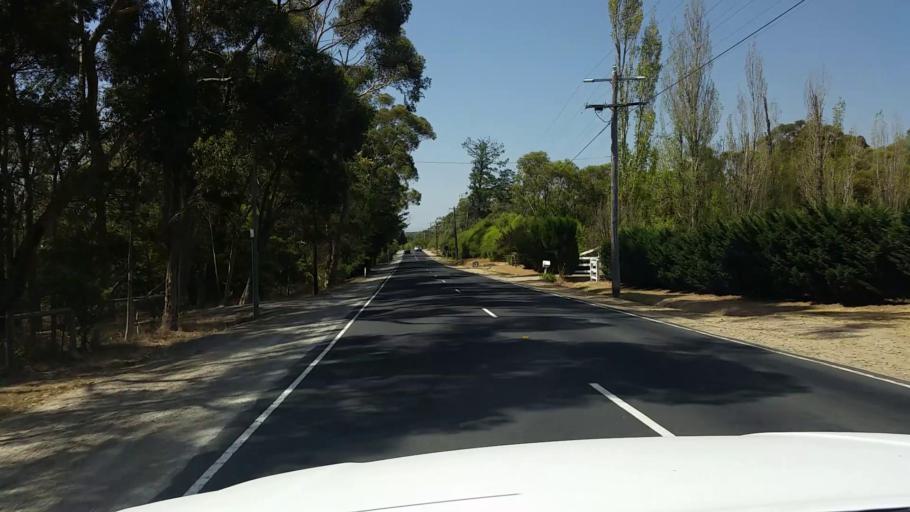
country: AU
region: Victoria
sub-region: Mornington Peninsula
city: Tyabb
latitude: -38.2607
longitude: 145.1616
